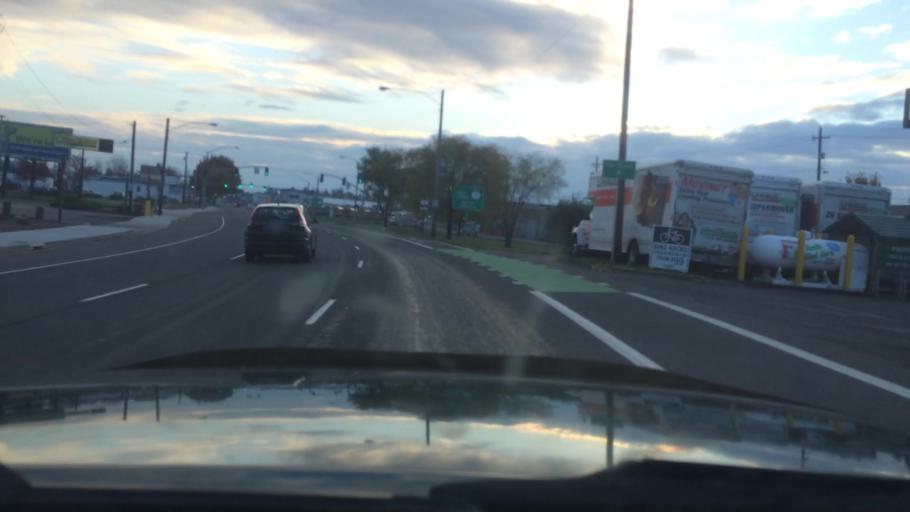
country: US
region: Oregon
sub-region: Lane County
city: Eugene
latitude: 44.0522
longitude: -123.1257
